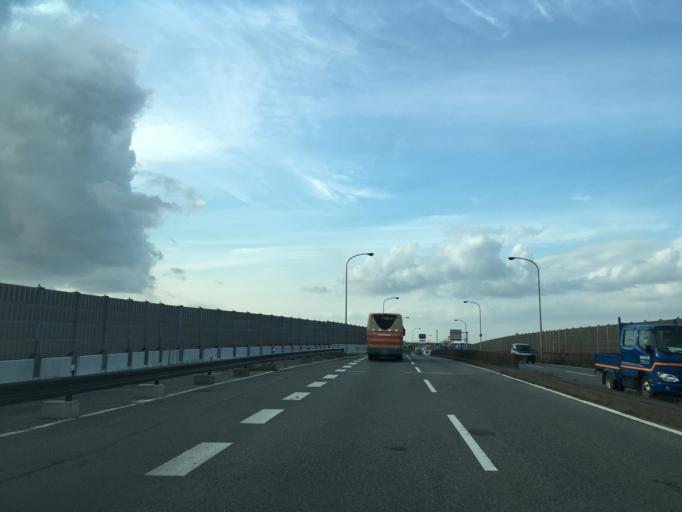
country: JP
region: Chiba
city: Kisarazu
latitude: 35.3901
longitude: 139.9409
